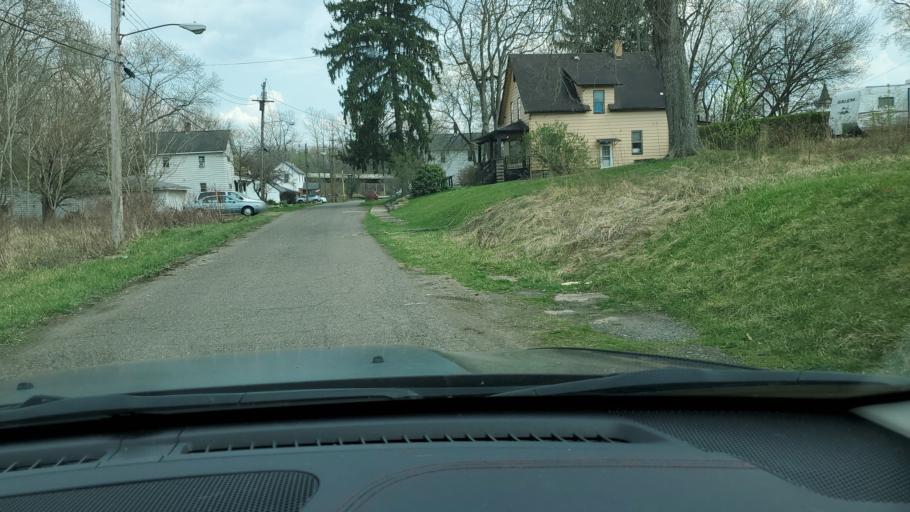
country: US
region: Ohio
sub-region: Trumbull County
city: Niles
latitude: 41.1772
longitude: -80.7680
